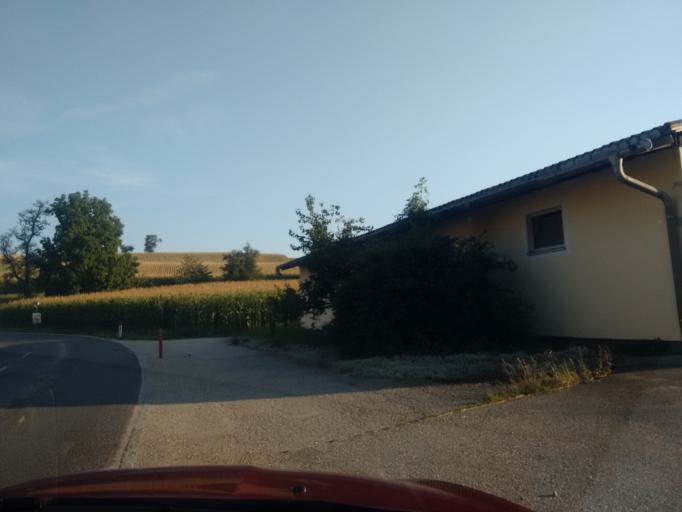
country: AT
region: Upper Austria
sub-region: Politischer Bezirk Vocklabruck
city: Wolfsegg am Hausruck
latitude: 48.1438
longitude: 13.7031
